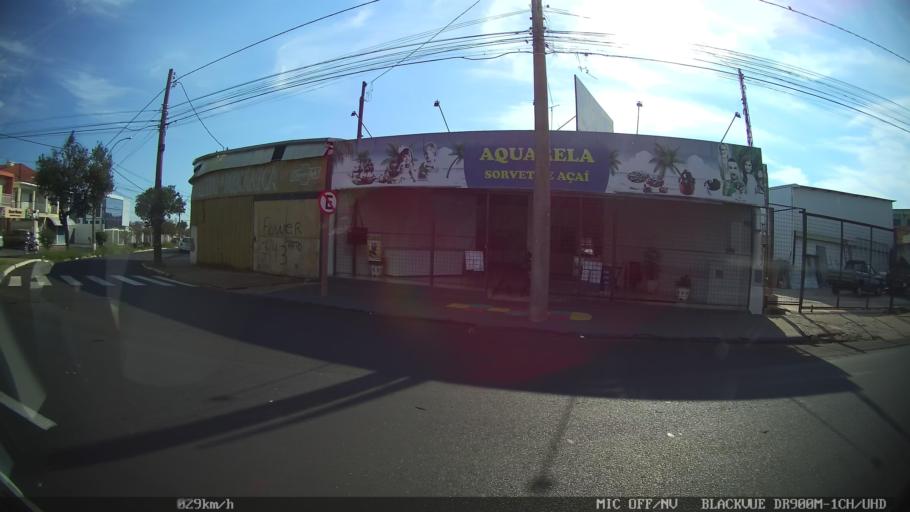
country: BR
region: Sao Paulo
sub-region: Araraquara
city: Araraquara
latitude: -21.7772
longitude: -48.1596
